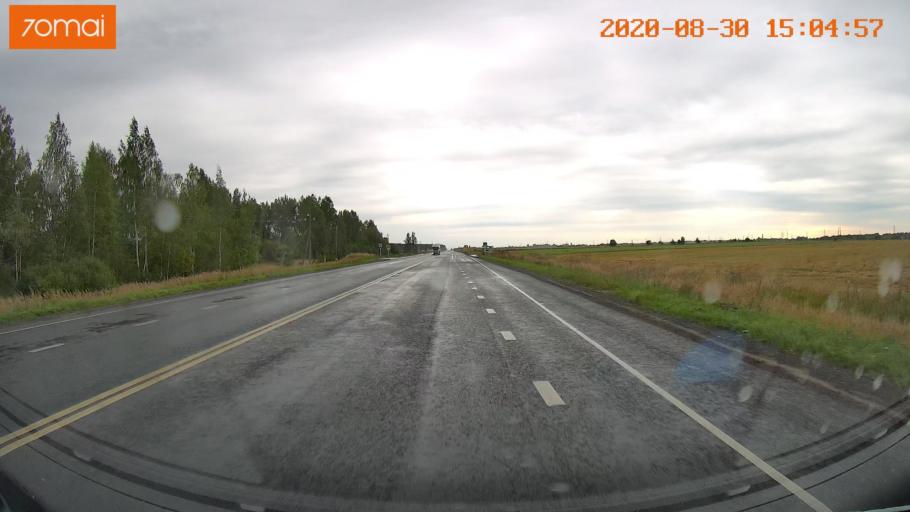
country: RU
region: Ivanovo
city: Staraya Vichuga
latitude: 57.2797
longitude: 41.9095
